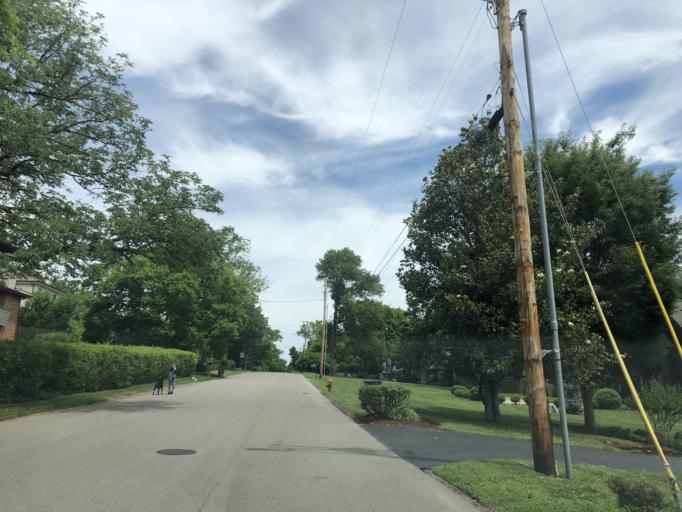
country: US
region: Tennessee
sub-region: Davidson County
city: Oak Hill
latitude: 36.1117
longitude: -86.8033
